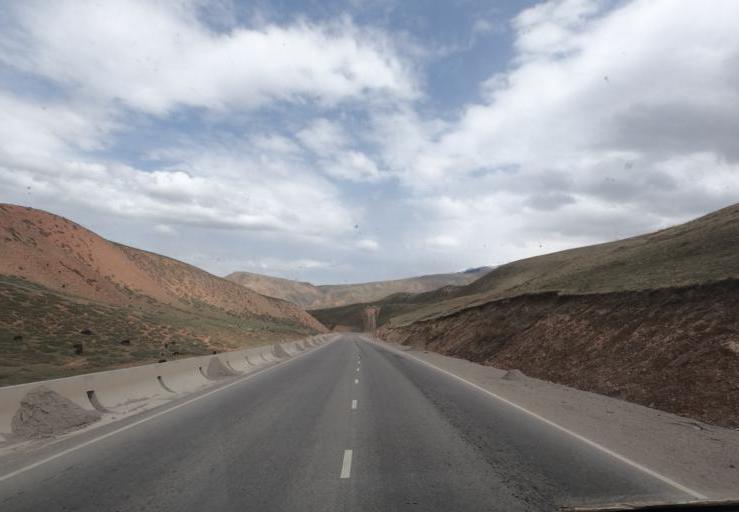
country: KG
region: Naryn
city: Naryn
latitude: 41.3808
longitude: 75.9890
